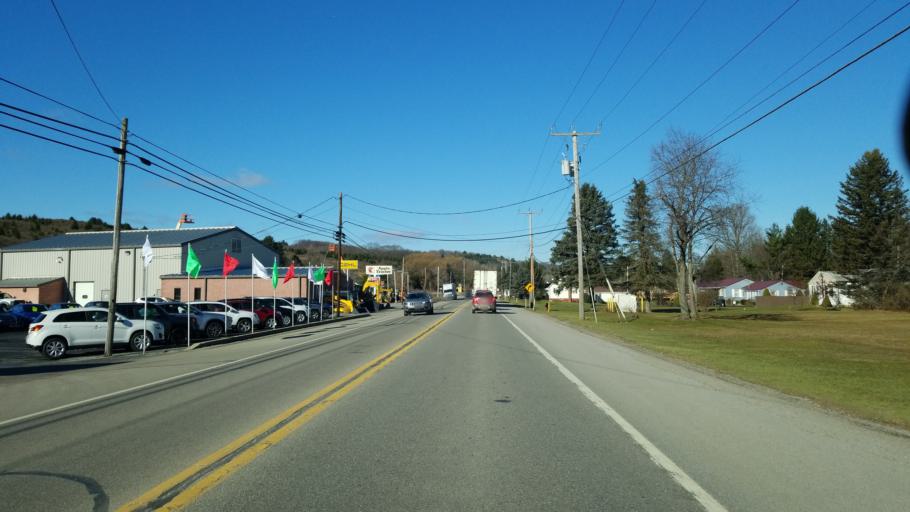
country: US
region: Pennsylvania
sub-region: Jefferson County
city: Brockway
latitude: 41.2242
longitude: -78.7787
